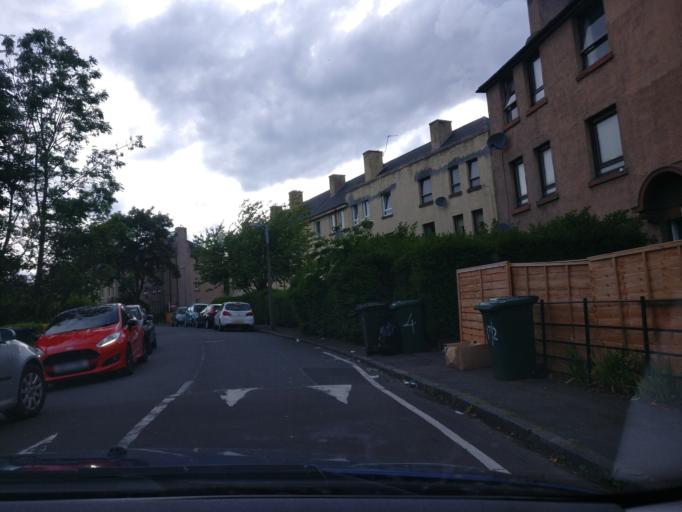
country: GB
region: Scotland
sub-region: West Lothian
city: Seafield
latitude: 55.9595
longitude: -3.1408
